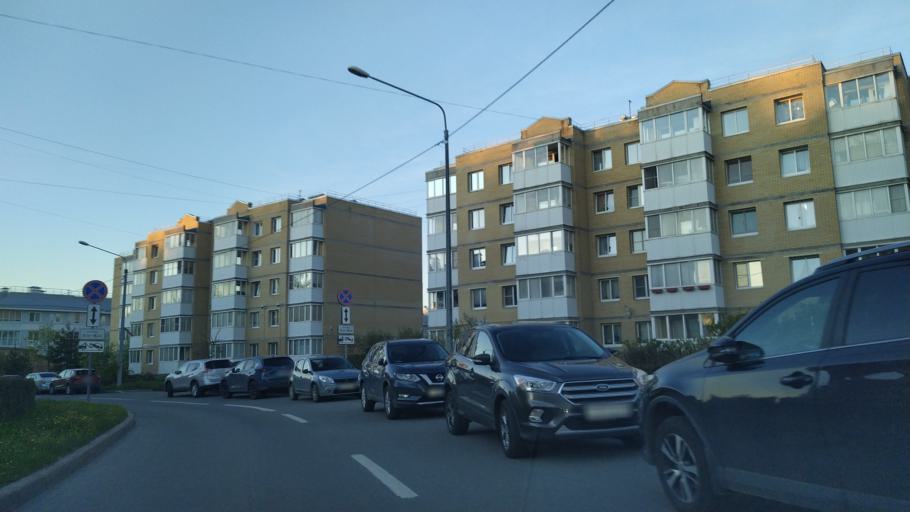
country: RU
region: St.-Petersburg
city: Pushkin
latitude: 59.7067
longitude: 30.3840
